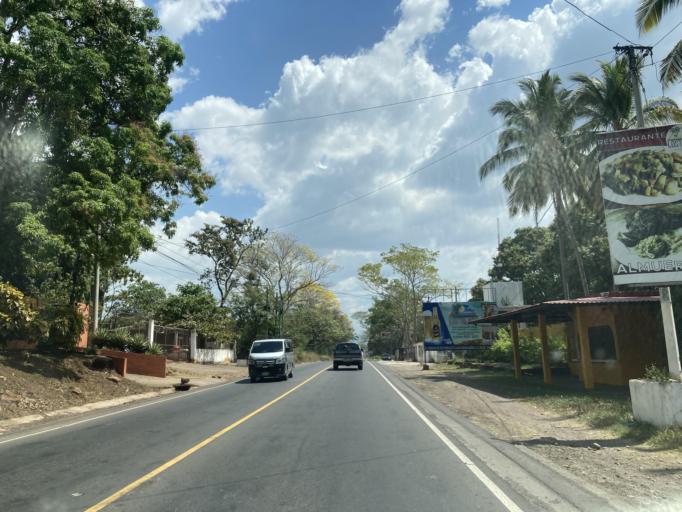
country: GT
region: Santa Rosa
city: Guazacapan
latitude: 14.0674
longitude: -90.3981
